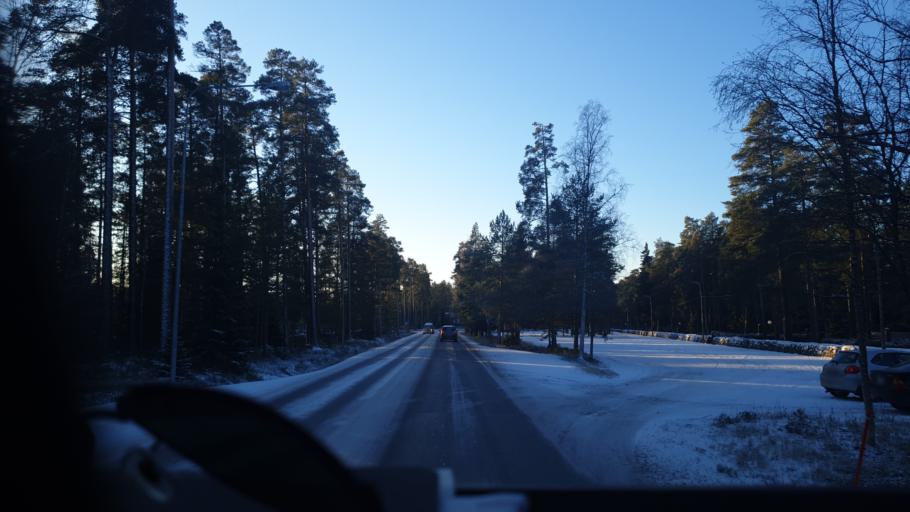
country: FI
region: Central Ostrobothnia
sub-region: Kokkola
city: Kokkola
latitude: 63.8286
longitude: 23.1021
